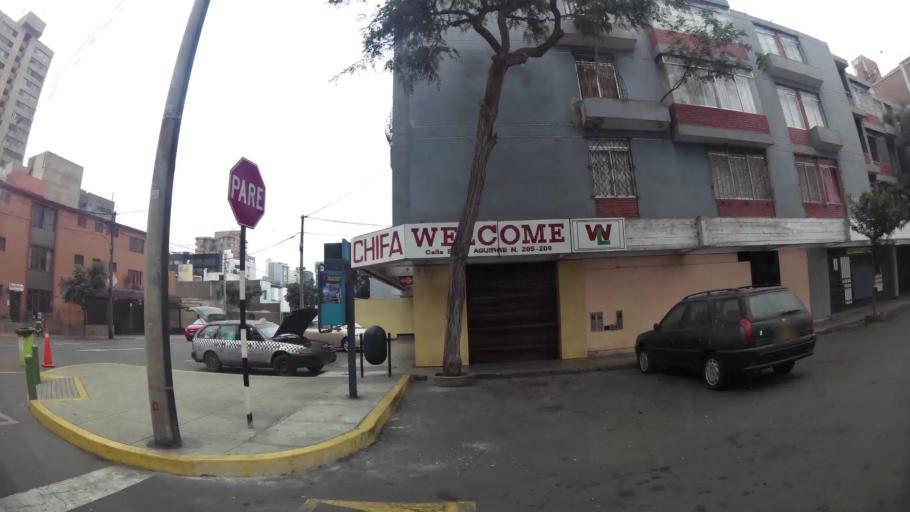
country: PE
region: Lima
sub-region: Lima
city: San Isidro
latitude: -12.1178
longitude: -77.0348
